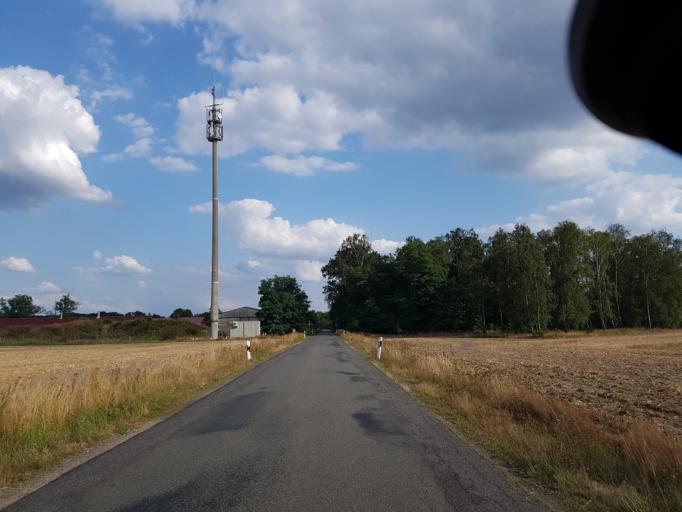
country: DE
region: Brandenburg
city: Bronkow
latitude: 51.6756
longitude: 13.9073
